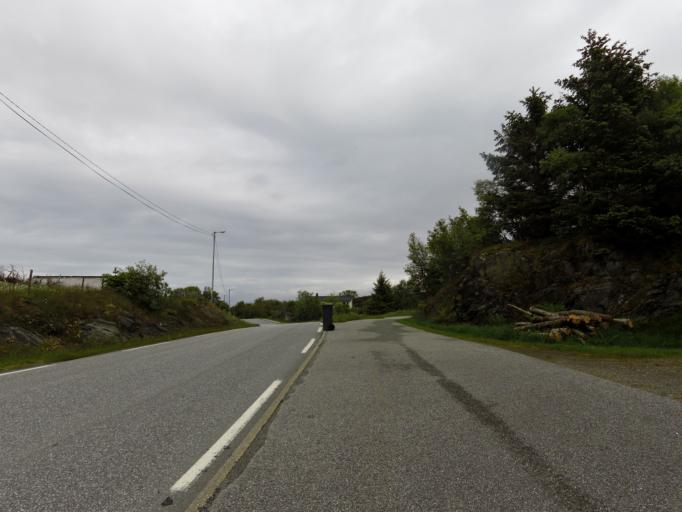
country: NO
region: Hordaland
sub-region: Sveio
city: Sveio
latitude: 59.6024
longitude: 5.2254
